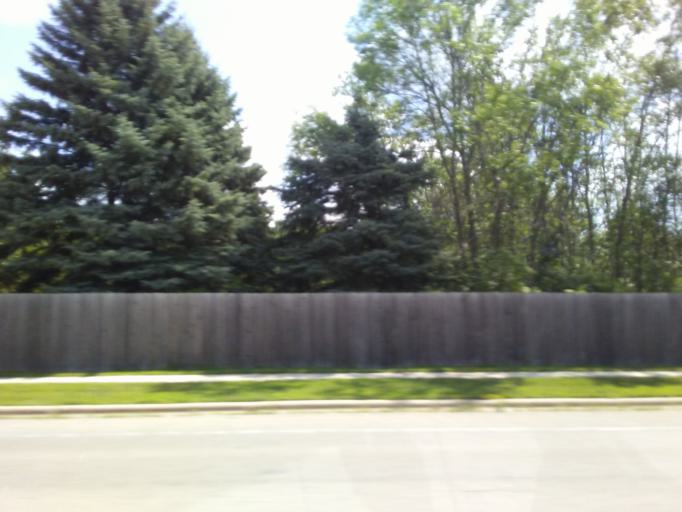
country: US
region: Wisconsin
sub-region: Dane County
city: Verona
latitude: 43.0423
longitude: -89.5181
